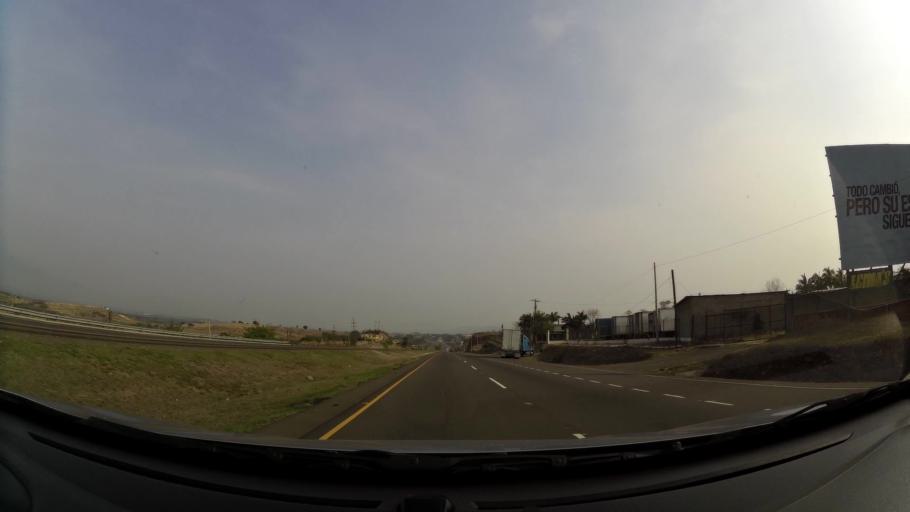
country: HN
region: Comayagua
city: Comayagua
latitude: 14.4064
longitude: -87.6206
